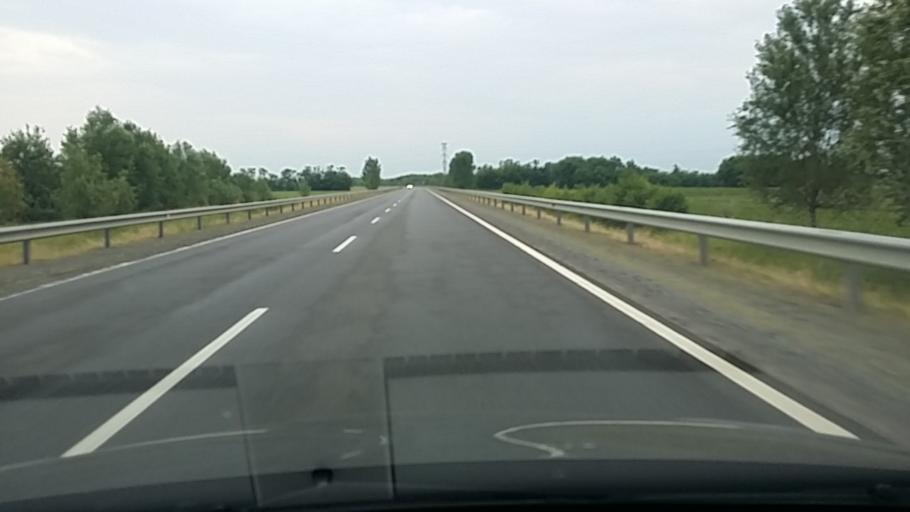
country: HU
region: Szabolcs-Szatmar-Bereg
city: Nyirpazony
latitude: 47.9673
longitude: 21.8163
